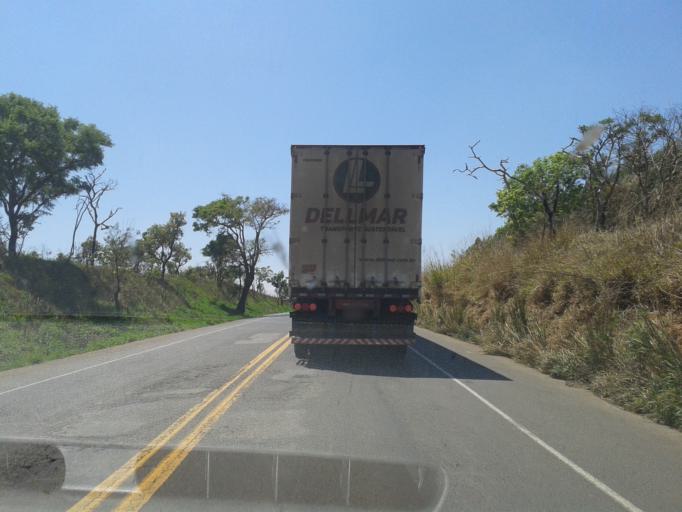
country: BR
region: Minas Gerais
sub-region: Araxa
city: Araxa
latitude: -19.4349
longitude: -47.2041
